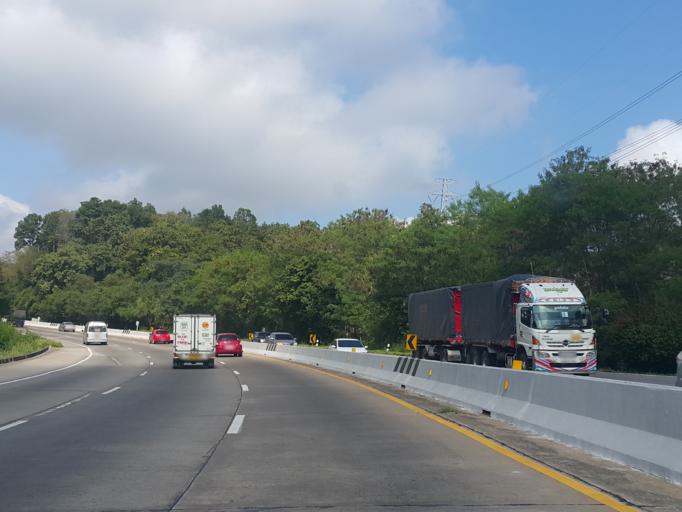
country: TH
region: Lampang
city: Hang Chat
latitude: 18.3582
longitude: 99.2412
